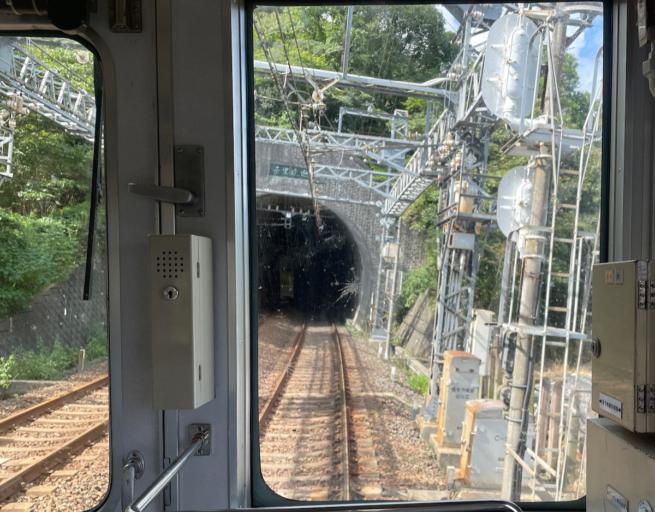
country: JP
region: Mie
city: Toba
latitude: 34.4280
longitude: 136.8282
